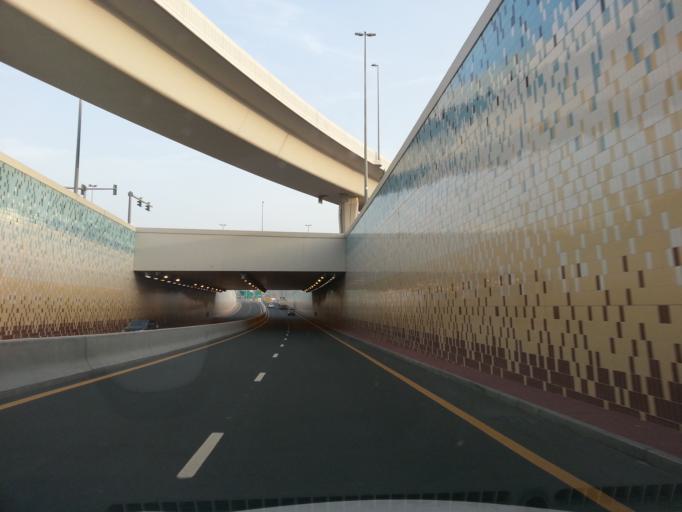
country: AE
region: Dubai
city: Dubai
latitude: 25.0565
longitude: 55.1399
